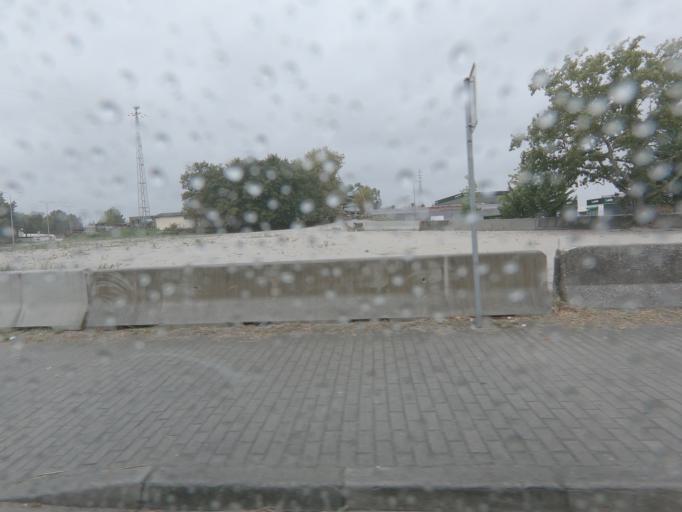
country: PT
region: Porto
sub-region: Paredes
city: Paredes
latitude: 41.1922
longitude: -8.3065
